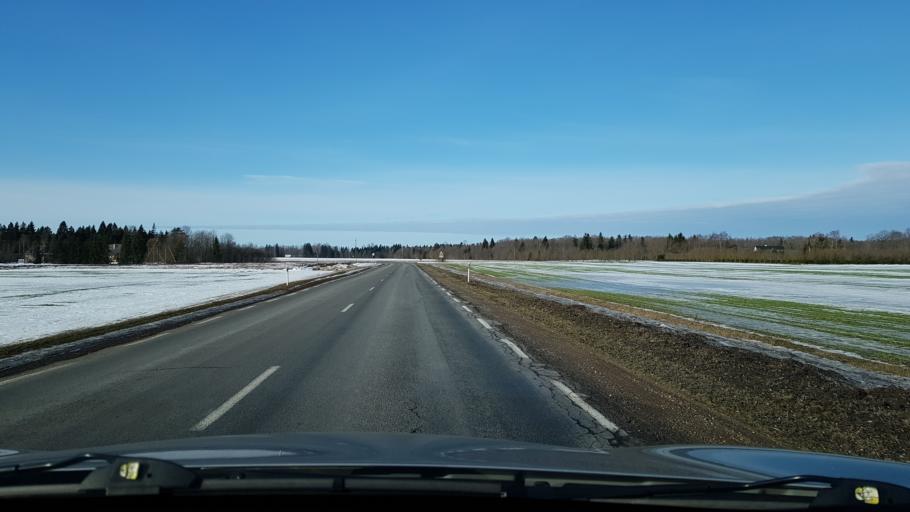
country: EE
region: Viljandimaa
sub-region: Vohma linn
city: Vohma
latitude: 58.6387
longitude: 25.6773
